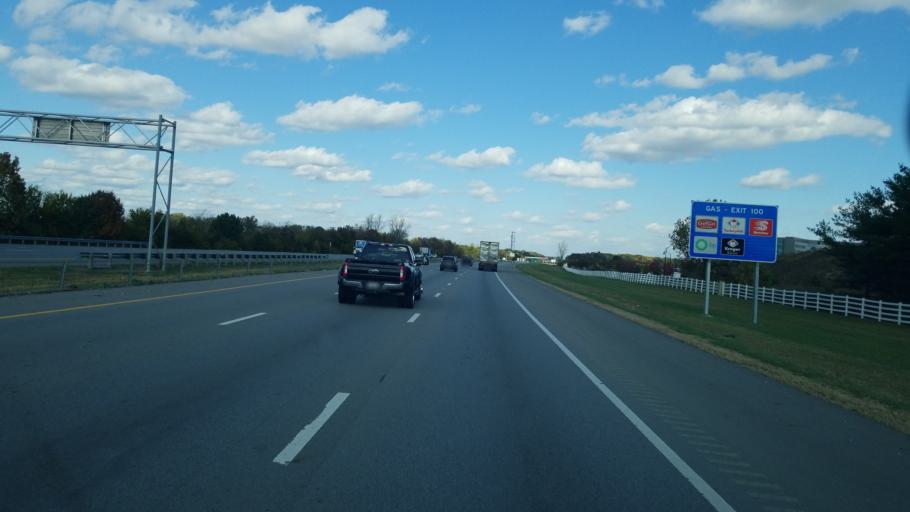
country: US
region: Ohio
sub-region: Franklin County
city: Grove City
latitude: 39.8499
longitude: -83.0836
